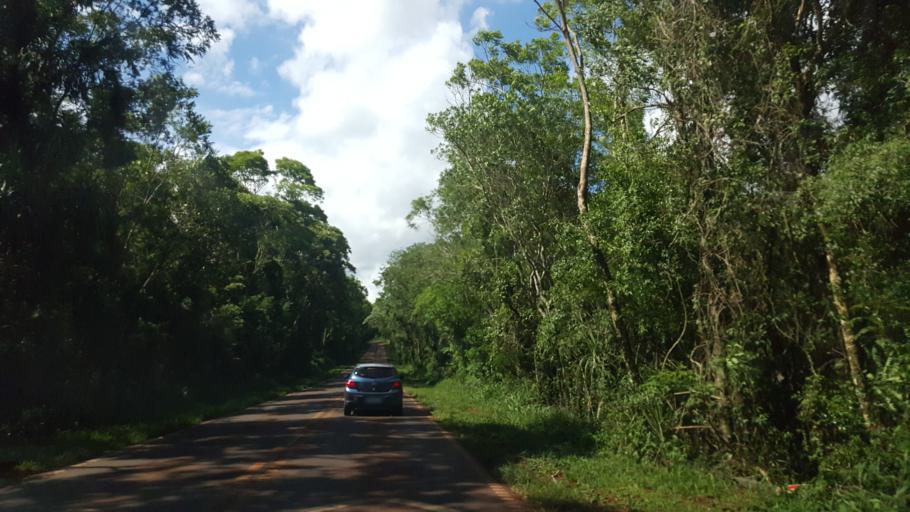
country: AR
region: Misiones
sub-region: Departamento de Iguazu
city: Puerto Iguazu
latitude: -25.7164
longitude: -54.4624
